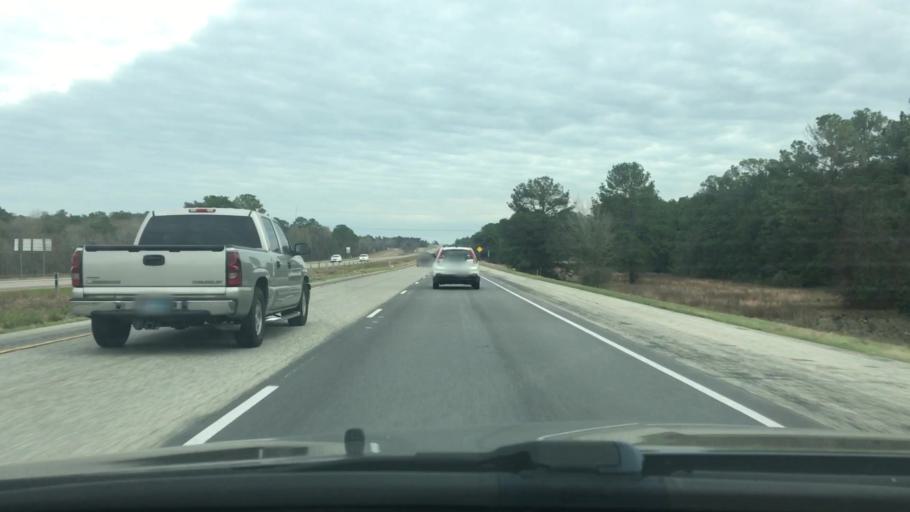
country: US
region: Texas
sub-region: Walker County
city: Huntsville
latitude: 30.7926
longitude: -95.6748
